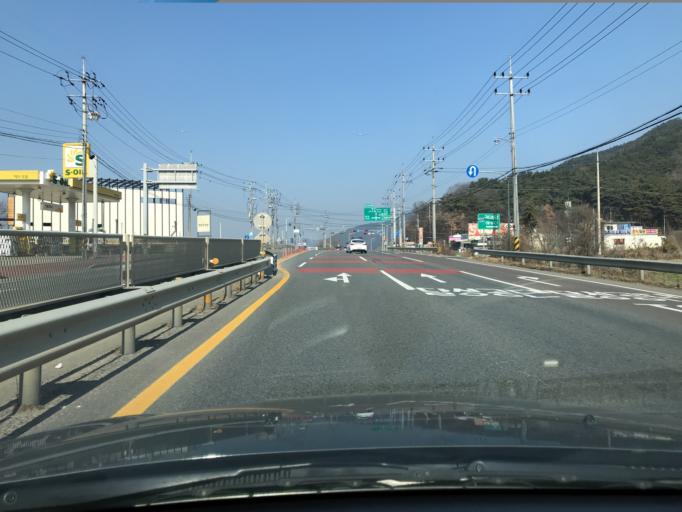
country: KR
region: Daegu
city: Hwawon
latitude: 35.7066
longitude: 128.4374
